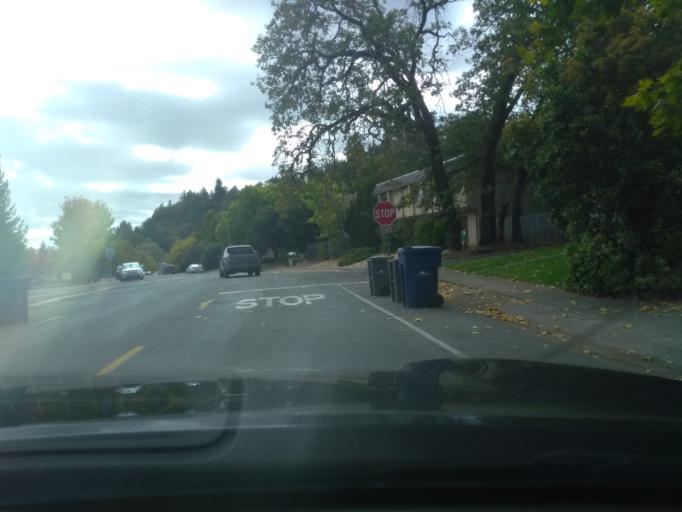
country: US
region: California
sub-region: Mendocino County
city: Ukiah
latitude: 39.1239
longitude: -123.2077
